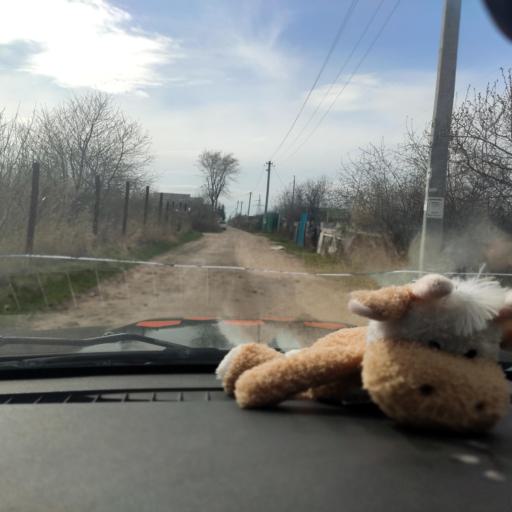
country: RU
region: Samara
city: Tol'yatti
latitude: 53.5935
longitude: 49.2435
